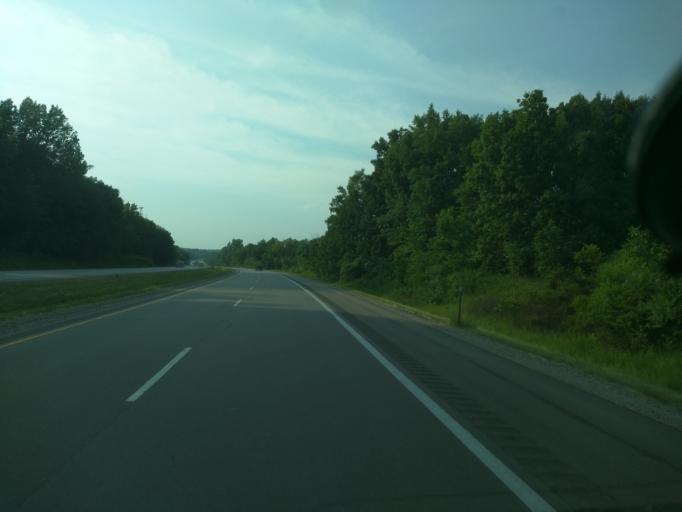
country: US
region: Michigan
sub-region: Ingham County
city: Leslie
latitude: 42.4180
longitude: -84.4304
